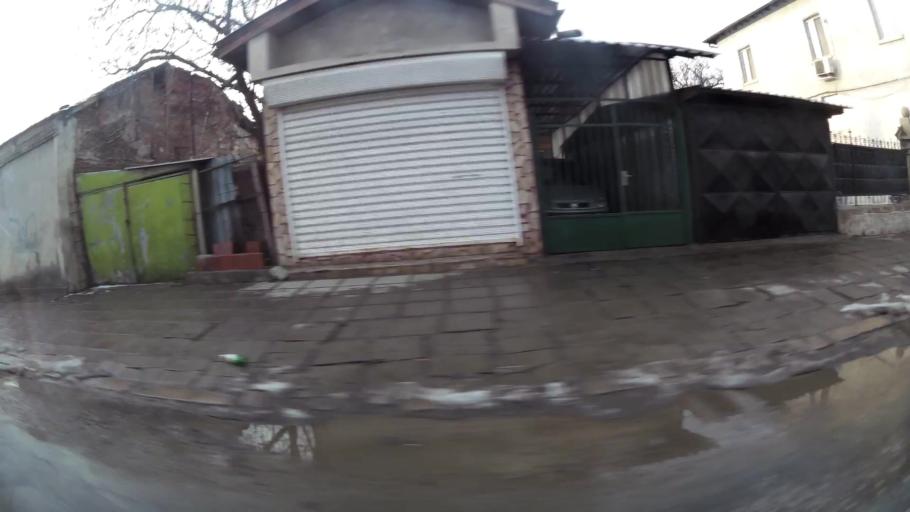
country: BG
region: Sofia-Capital
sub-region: Stolichna Obshtina
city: Sofia
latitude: 42.7248
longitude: 23.3440
